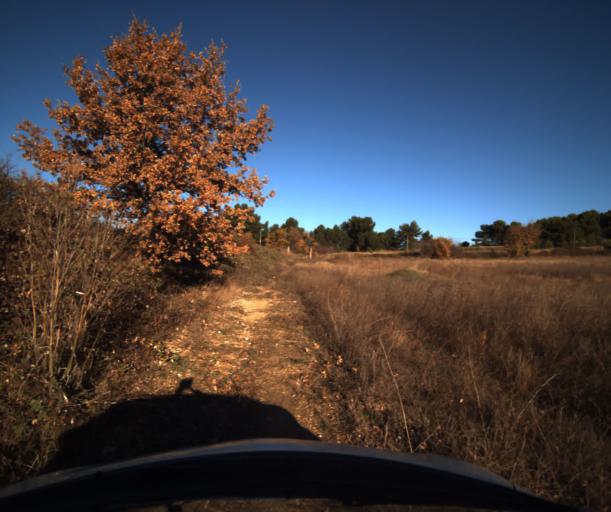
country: FR
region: Provence-Alpes-Cote d'Azur
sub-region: Departement du Vaucluse
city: Ansouis
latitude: 43.7239
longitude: 5.4927
